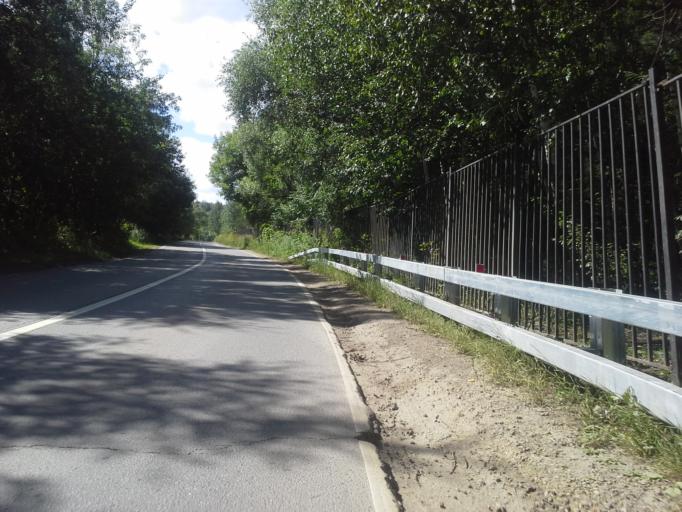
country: RU
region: Moskovskaya
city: Zarech'ye
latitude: 55.6645
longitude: 37.3861
